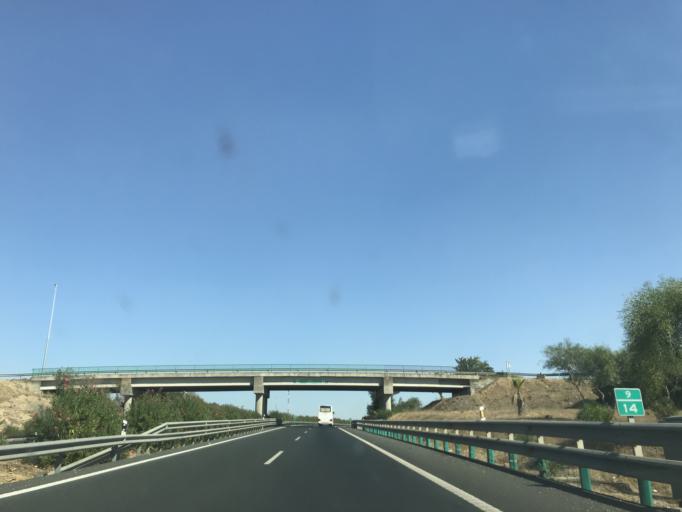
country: ES
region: Andalusia
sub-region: Provincia de Sevilla
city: Alcala de Guadaira
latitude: 37.3272
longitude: -5.8060
